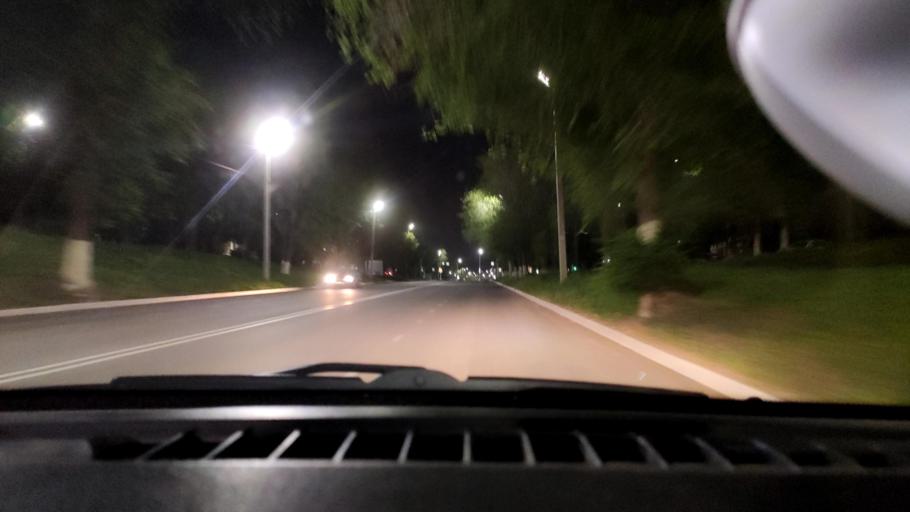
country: RU
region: Samara
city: Novokuybyshevsk
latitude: 53.0978
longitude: 49.9747
